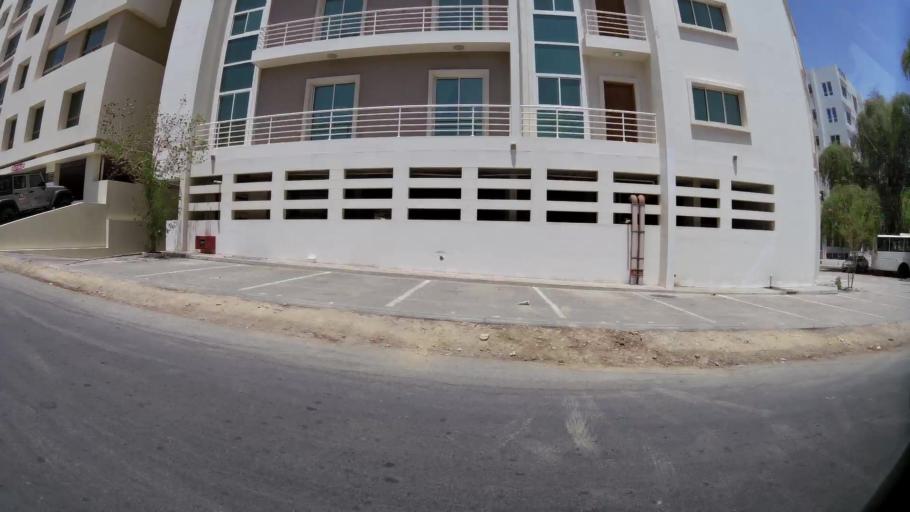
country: OM
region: Muhafazat Masqat
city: Muscat
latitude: 23.6207
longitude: 58.5004
